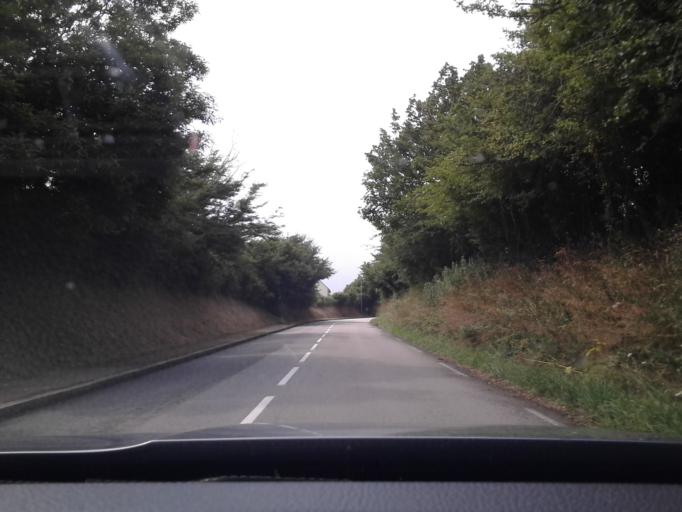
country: FR
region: Lower Normandy
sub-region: Departement de la Manche
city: Beaumont-Hague
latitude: 49.6740
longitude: -1.7926
